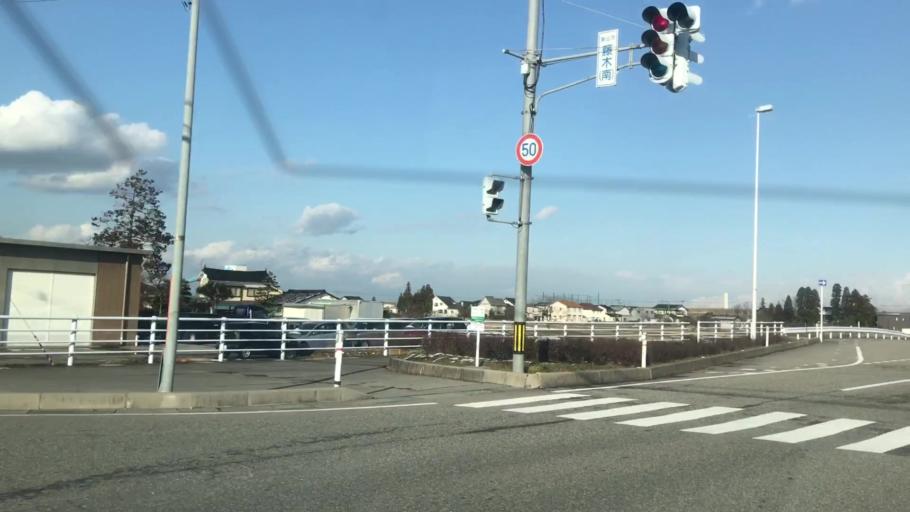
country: JP
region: Toyama
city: Toyama-shi
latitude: 36.6847
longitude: 137.2720
